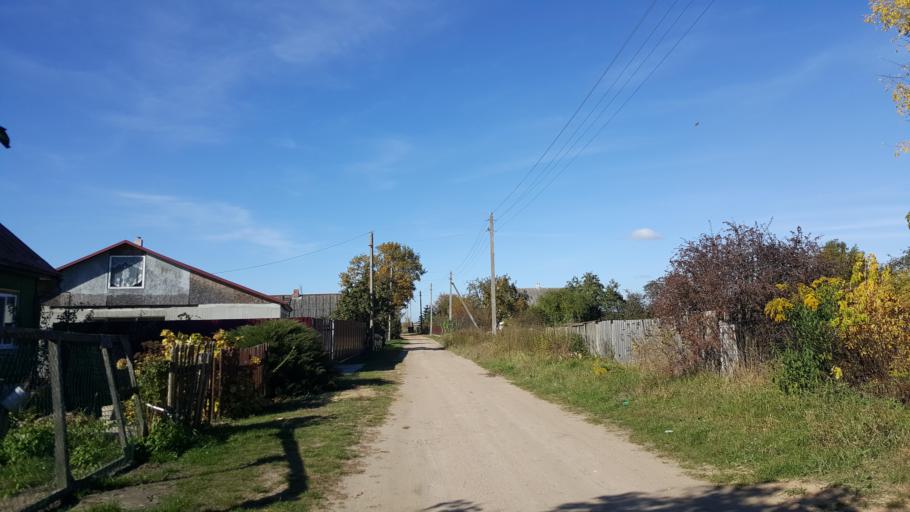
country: BY
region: Brest
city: Kamyanyets
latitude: 52.4047
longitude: 23.7891
